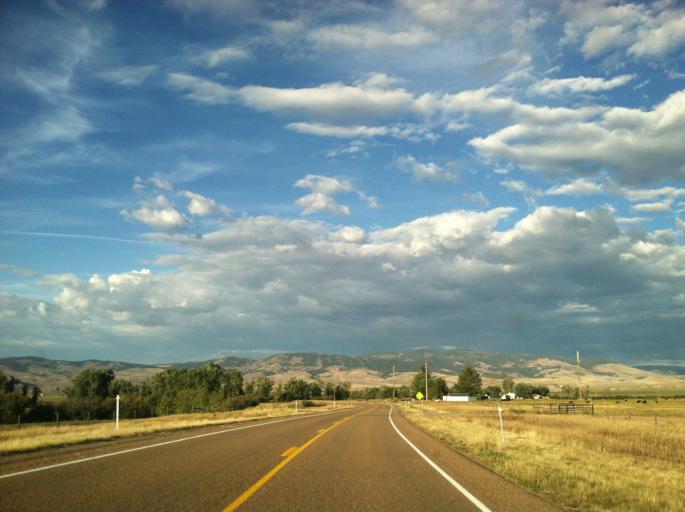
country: US
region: Montana
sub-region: Granite County
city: Philipsburg
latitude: 46.6087
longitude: -113.1831
